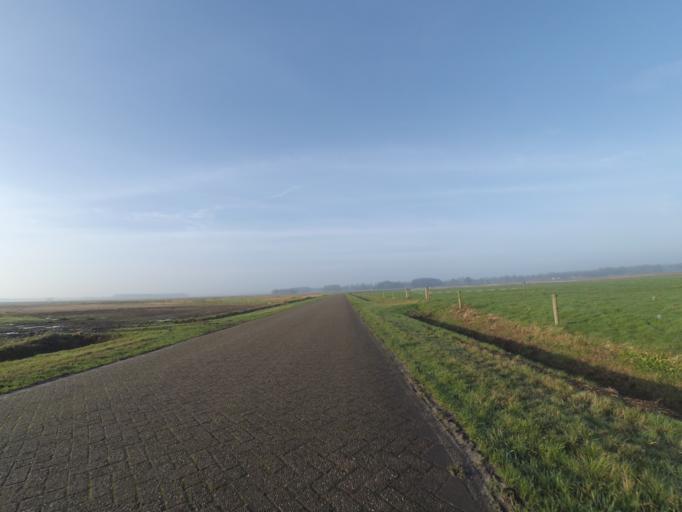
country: NL
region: Drenthe
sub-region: Gemeente Borger-Odoorn
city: Borger
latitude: 52.9034
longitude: 6.7867
